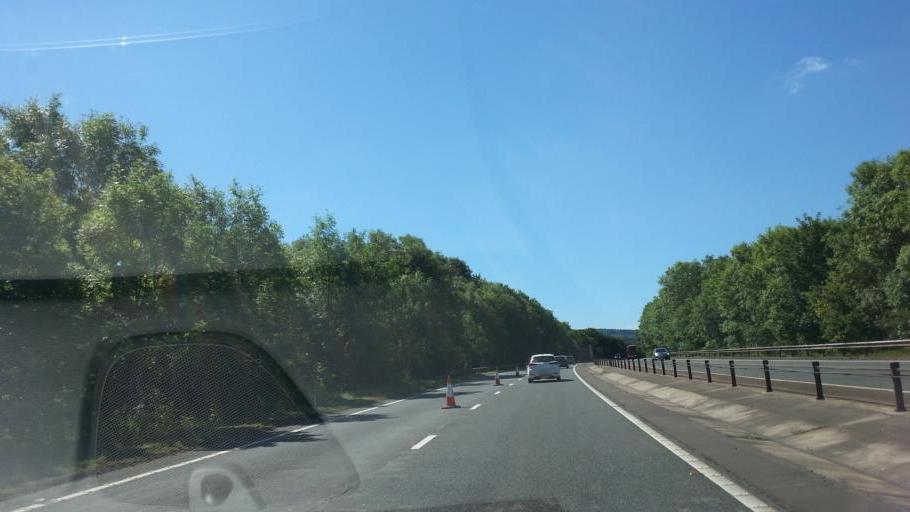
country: GB
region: Wales
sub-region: Monmouthshire
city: Llanbadoc
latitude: 51.6820
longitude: -2.8761
